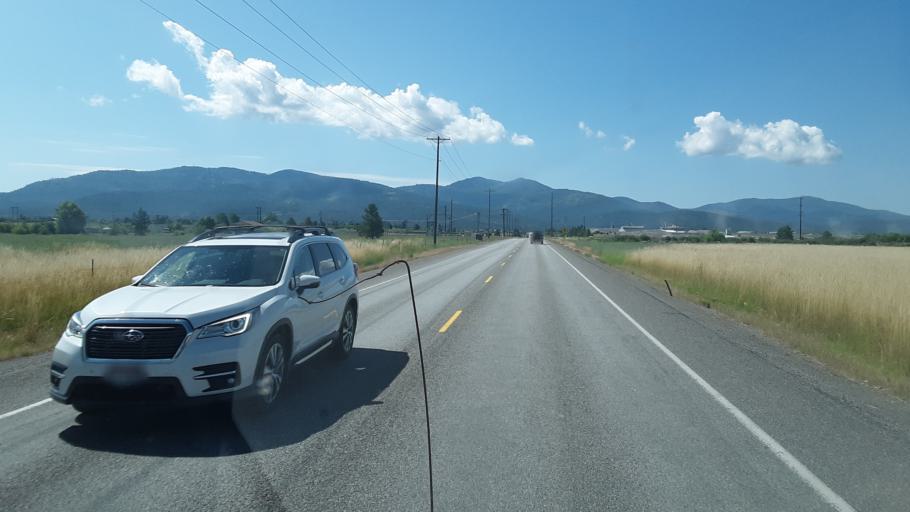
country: US
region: Idaho
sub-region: Kootenai County
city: Post Falls
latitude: 47.7343
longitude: -117.0021
